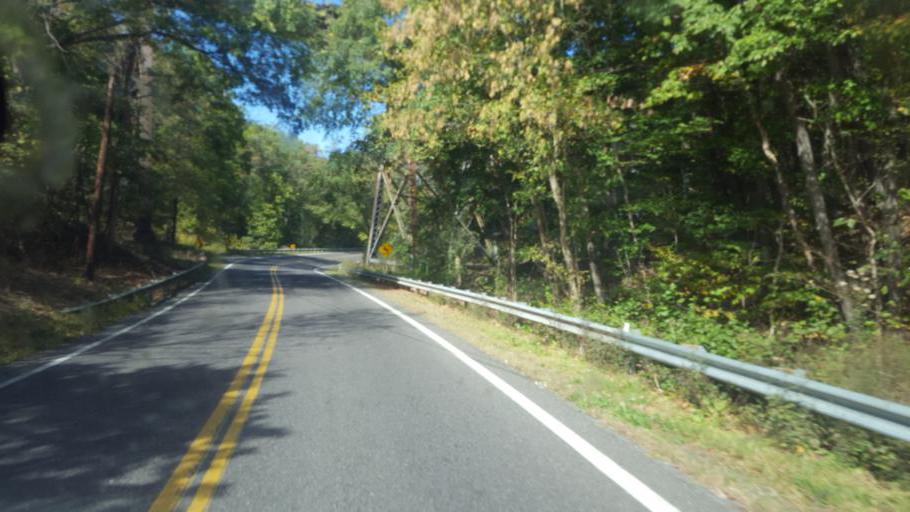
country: US
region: Virginia
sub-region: Page County
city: Luray
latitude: 38.7961
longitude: -78.3601
